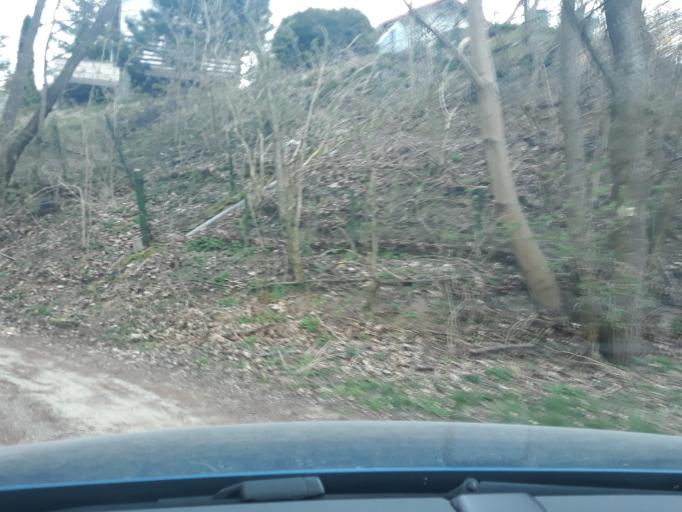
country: PL
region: Pomeranian Voivodeship
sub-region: Powiat chojnicki
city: Chojnice
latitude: 53.7265
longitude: 17.4927
